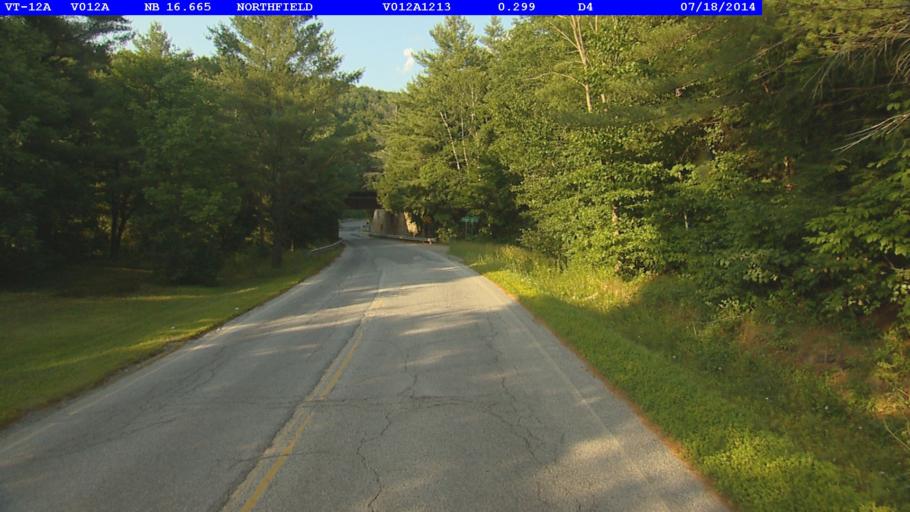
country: US
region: Vermont
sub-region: Washington County
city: Northfield
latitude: 44.1165
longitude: -72.7197
